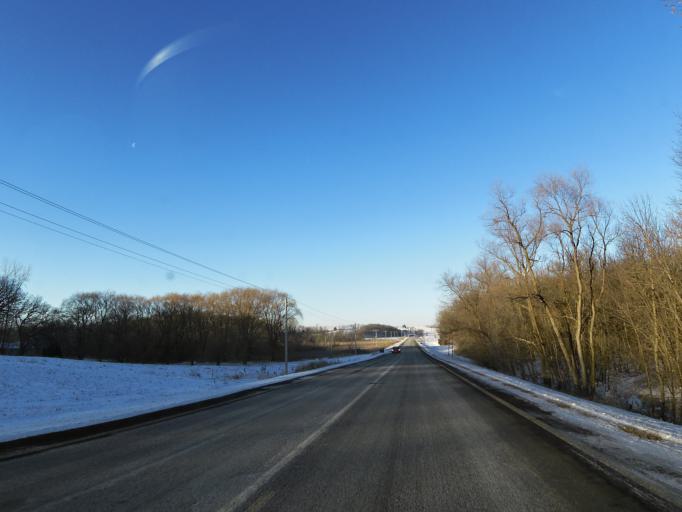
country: US
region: Minnesota
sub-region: Le Sueur County
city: New Prague
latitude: 44.6306
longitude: -93.5338
